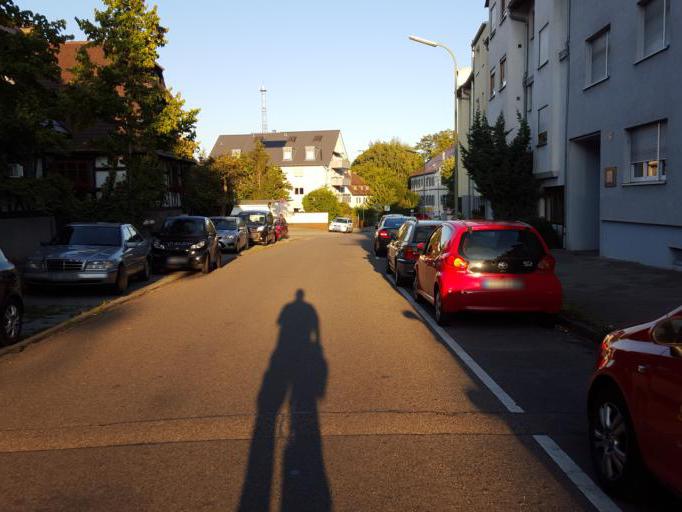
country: DE
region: Baden-Wuerttemberg
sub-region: Karlsruhe Region
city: Karlsruhe
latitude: 48.9914
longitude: 8.3902
